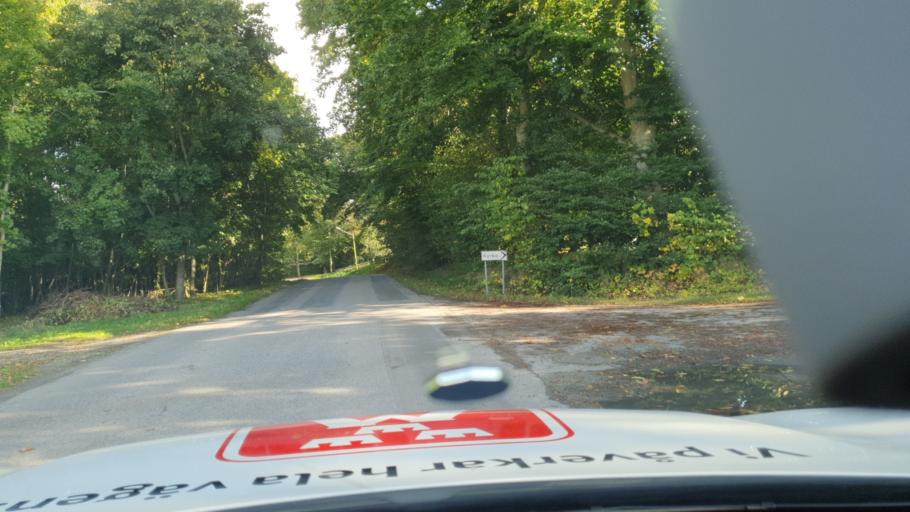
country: SE
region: Skane
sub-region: Tomelilla Kommun
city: Tomelilla
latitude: 55.5048
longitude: 13.9509
